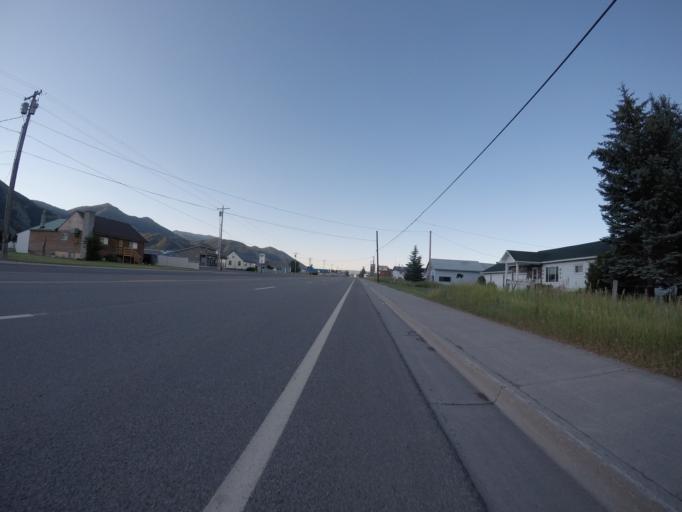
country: US
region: Wyoming
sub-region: Lincoln County
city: Afton
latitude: 42.7413
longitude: -110.9335
